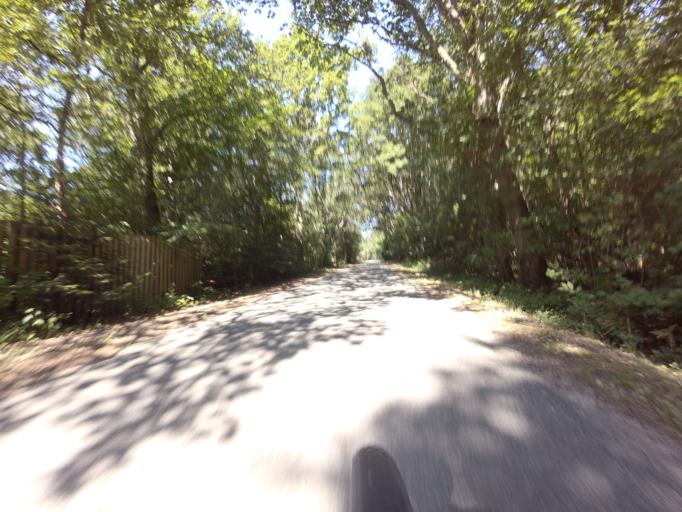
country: DK
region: North Denmark
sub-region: Laeso Kommune
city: Byrum
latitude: 57.2732
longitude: 11.0115
